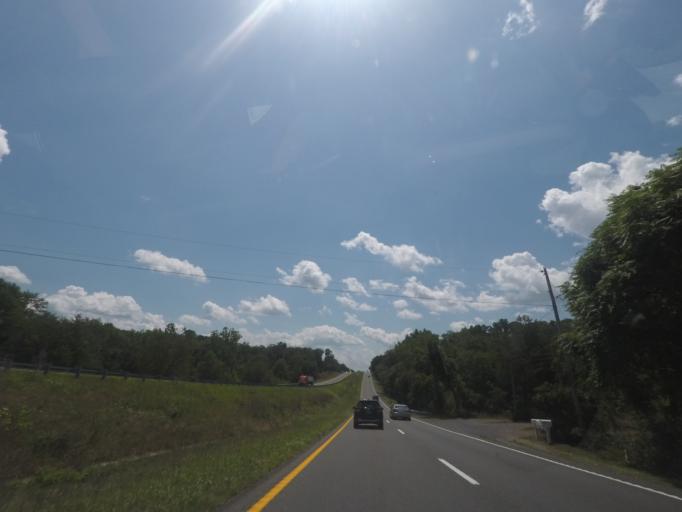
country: US
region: Virginia
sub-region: City of Winchester
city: Winchester
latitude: 39.1267
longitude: -78.1197
